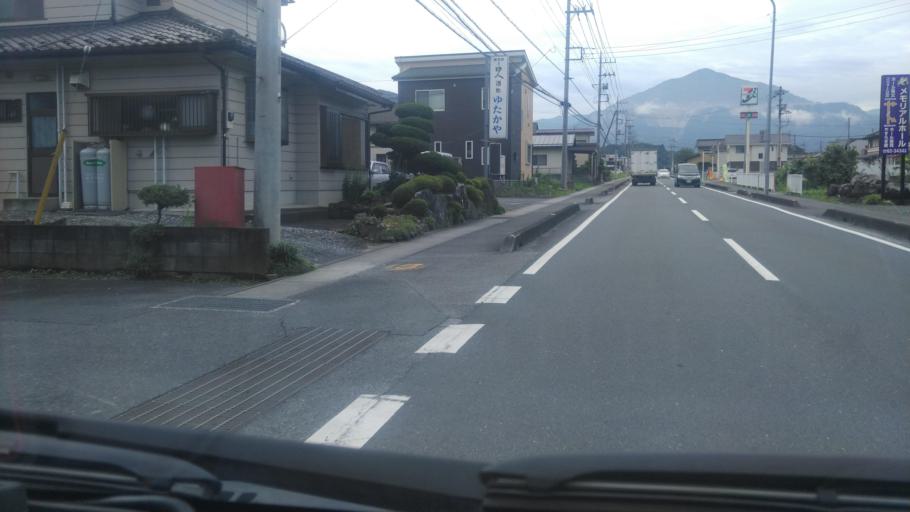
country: JP
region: Saitama
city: Chichibu
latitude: 36.0178
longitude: 139.1127
